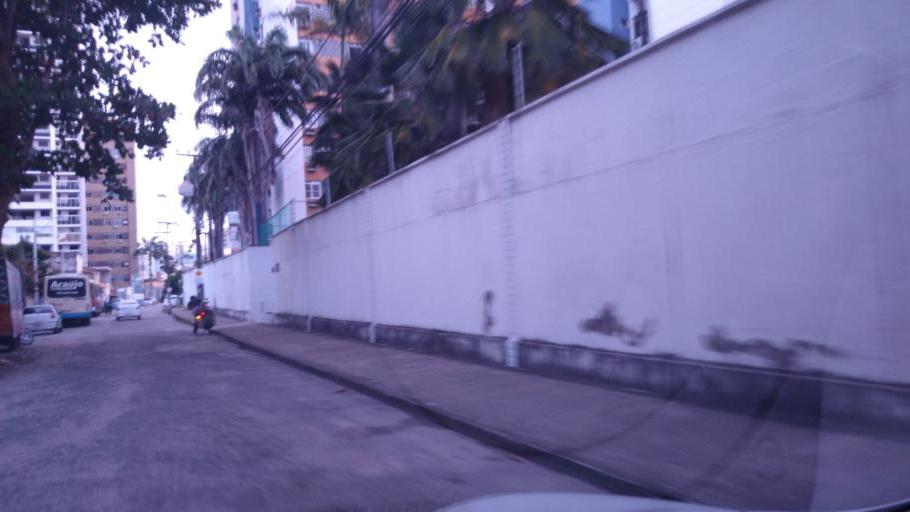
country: BR
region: Ceara
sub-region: Fortaleza
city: Fortaleza
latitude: -3.7272
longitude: -38.4879
